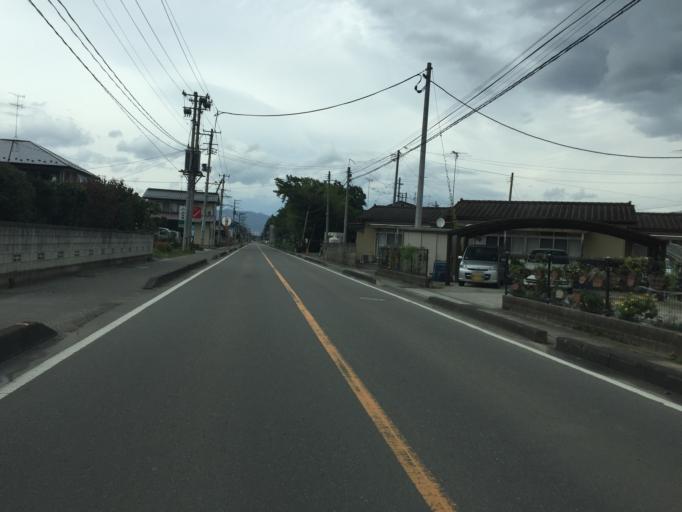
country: JP
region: Fukushima
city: Hobaramachi
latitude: 37.8276
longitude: 140.5566
